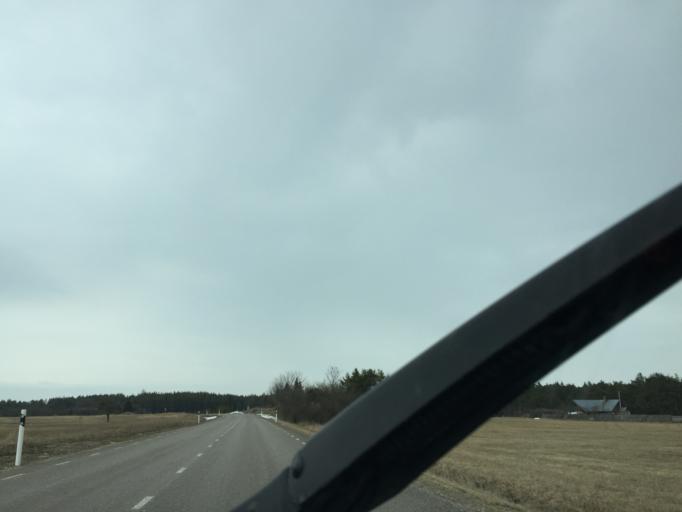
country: EE
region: Saare
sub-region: Orissaare vald
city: Orissaare
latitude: 58.5839
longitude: 22.7062
